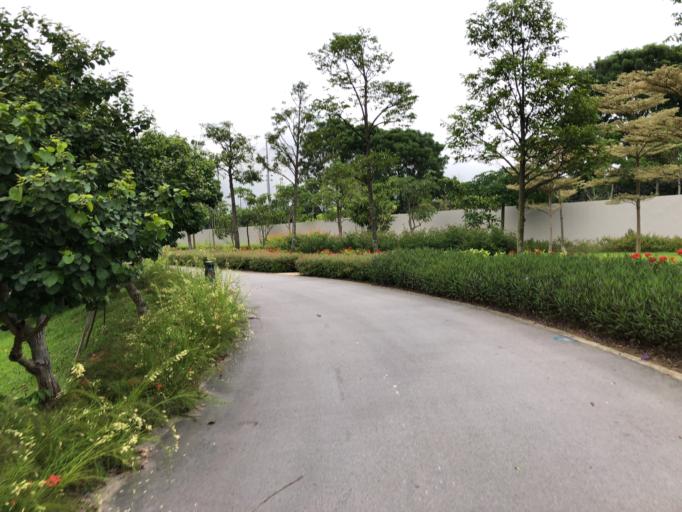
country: SG
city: Singapore
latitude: 1.2830
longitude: 103.8740
